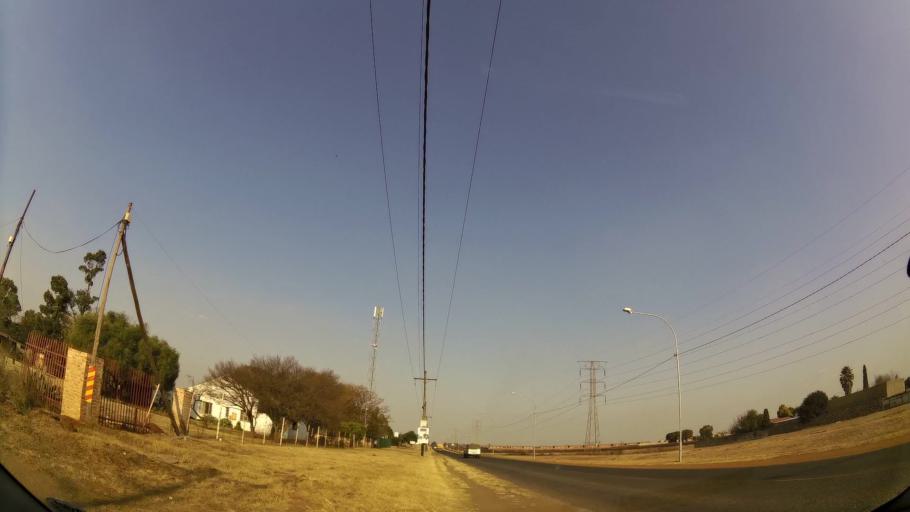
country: ZA
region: Gauteng
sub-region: Ekurhuleni Metropolitan Municipality
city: Benoni
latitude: -26.1218
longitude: 28.3803
